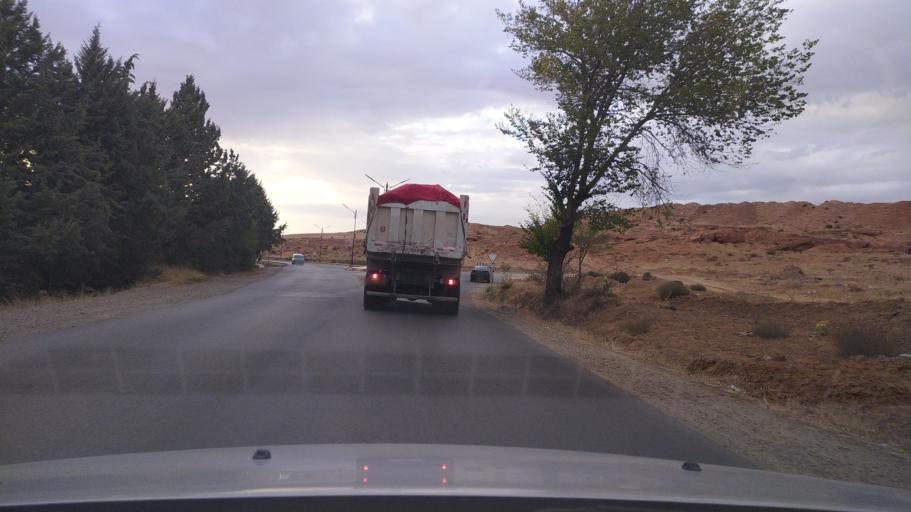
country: DZ
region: Tiaret
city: Frenda
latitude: 35.0505
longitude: 1.0752
